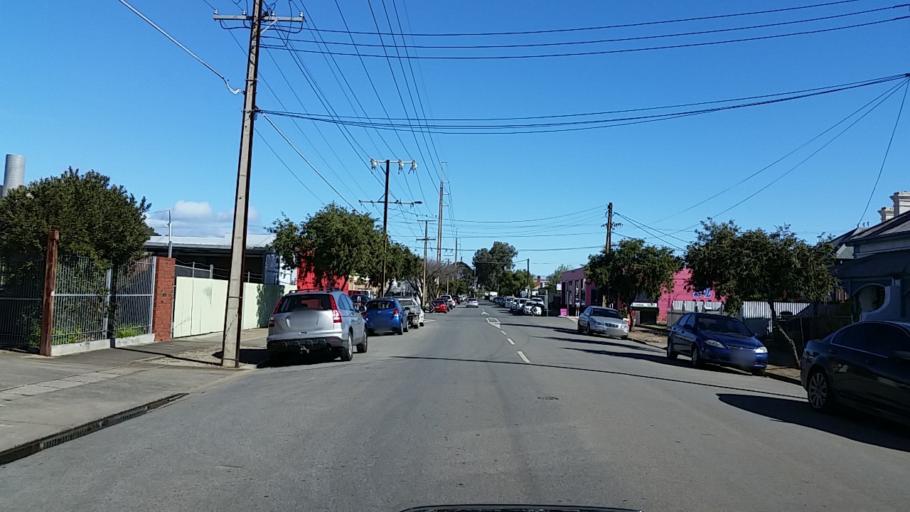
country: AU
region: South Australia
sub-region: City of West Torrens
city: Thebarton
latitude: -34.9074
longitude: 138.5667
